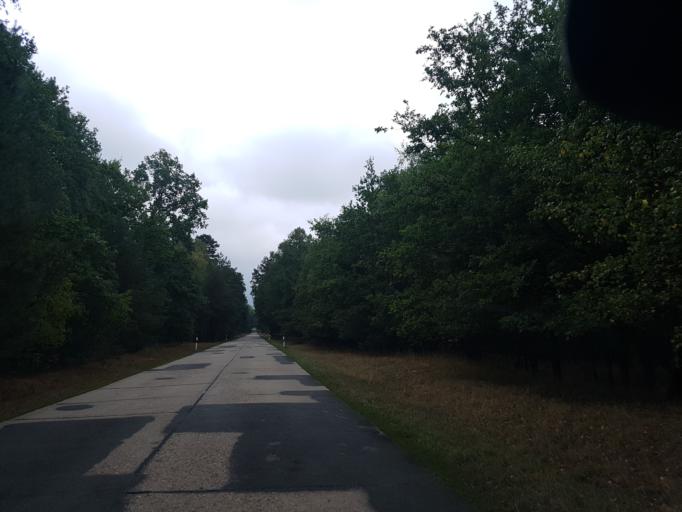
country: DE
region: Saxony-Anhalt
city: Lindau
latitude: 52.0648
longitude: 12.2529
